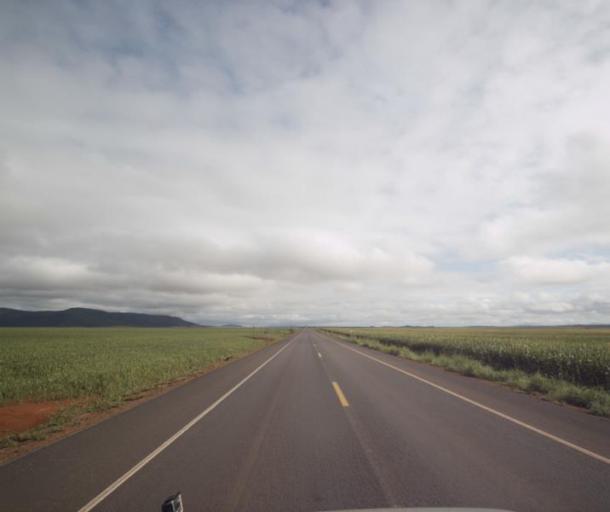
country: BR
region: Goias
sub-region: Padre Bernardo
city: Padre Bernardo
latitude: -15.4125
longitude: -48.6266
